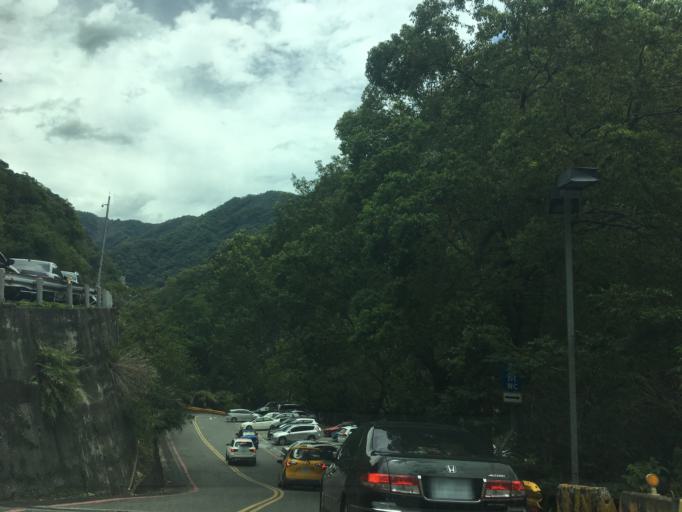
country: TW
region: Taiwan
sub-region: Hualien
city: Hualian
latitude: 24.1866
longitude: 121.4900
